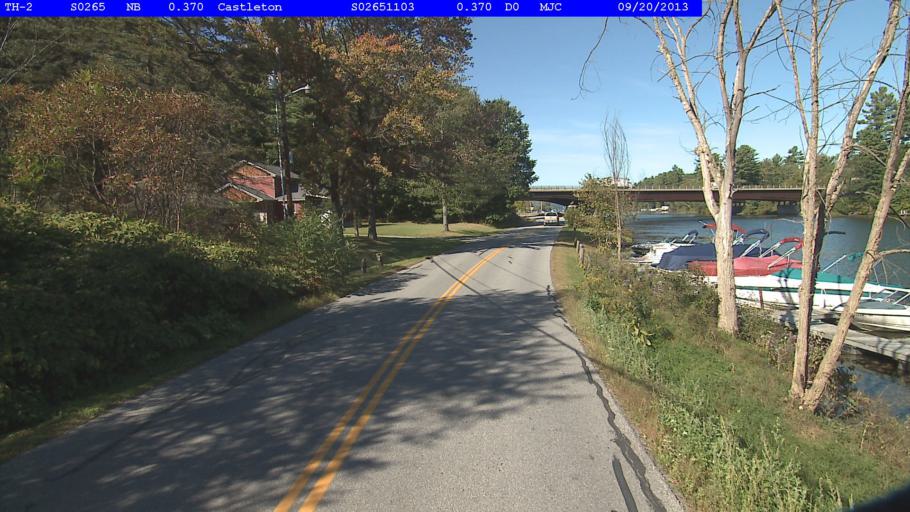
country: US
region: Vermont
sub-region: Rutland County
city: Fair Haven
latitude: 43.6098
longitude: -73.2328
